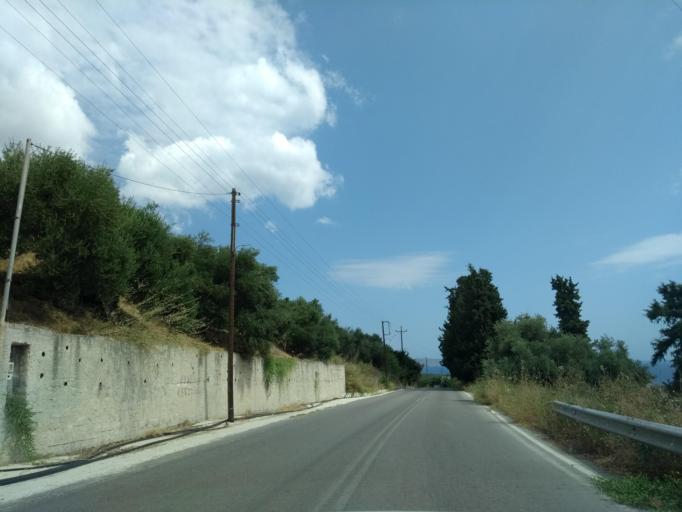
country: GR
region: Crete
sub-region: Nomos Chanias
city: Kalivai
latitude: 35.4360
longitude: 24.1755
